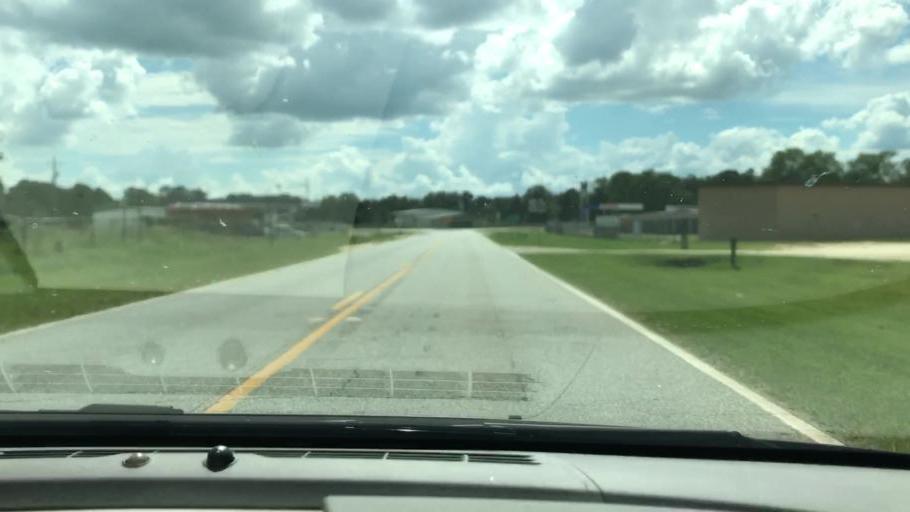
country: US
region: Georgia
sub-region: Quitman County
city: Georgetown
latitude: 31.8843
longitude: -85.0922
